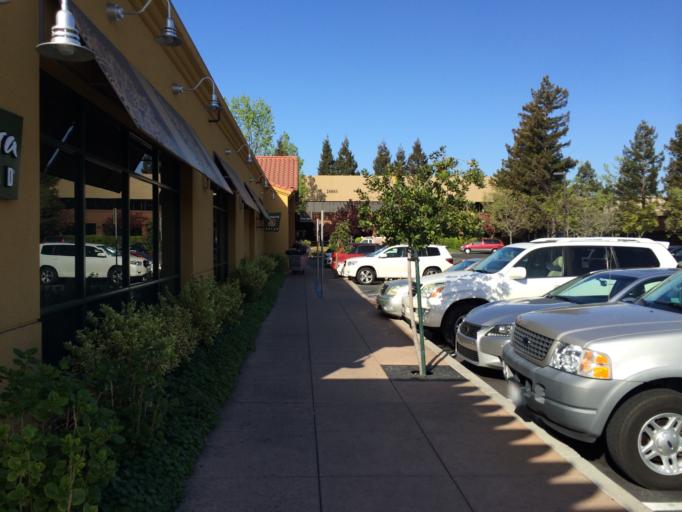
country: US
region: California
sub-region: Santa Clara County
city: Cupertino
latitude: 37.3233
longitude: -122.0379
